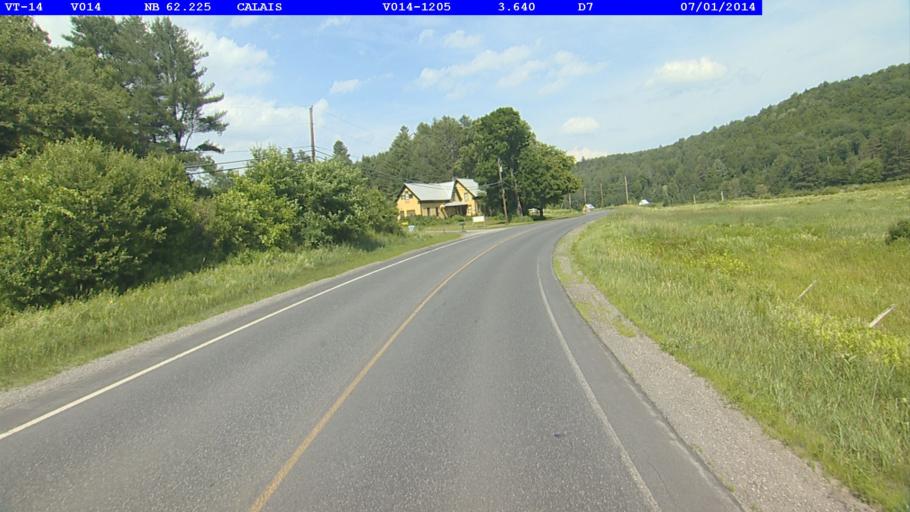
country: US
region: Vermont
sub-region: Washington County
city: Montpelier
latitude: 44.3578
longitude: -72.4439
